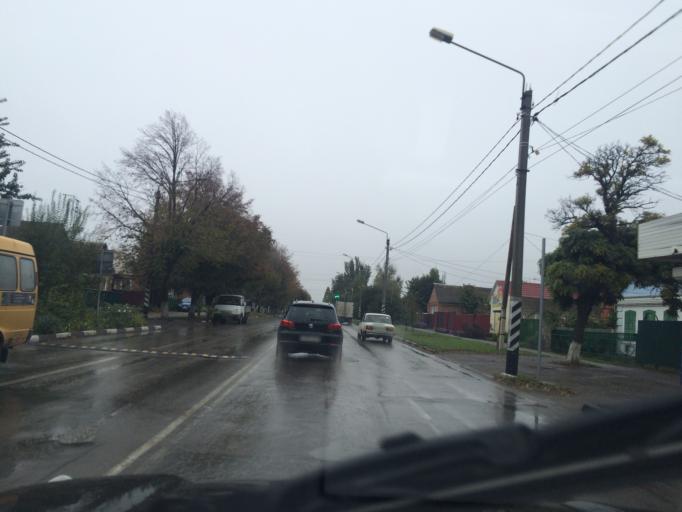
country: RU
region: Rostov
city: Azov
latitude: 47.0933
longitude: 39.4496
